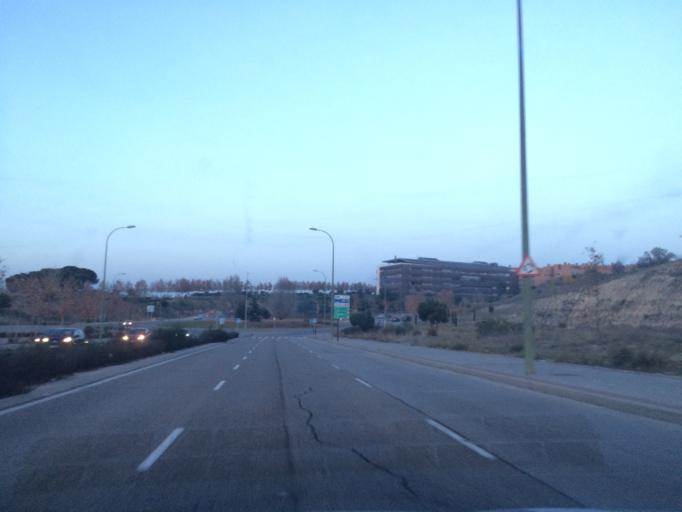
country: ES
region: Madrid
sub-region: Provincia de Madrid
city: Fuencarral-El Pardo
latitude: 40.5018
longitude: -3.7139
